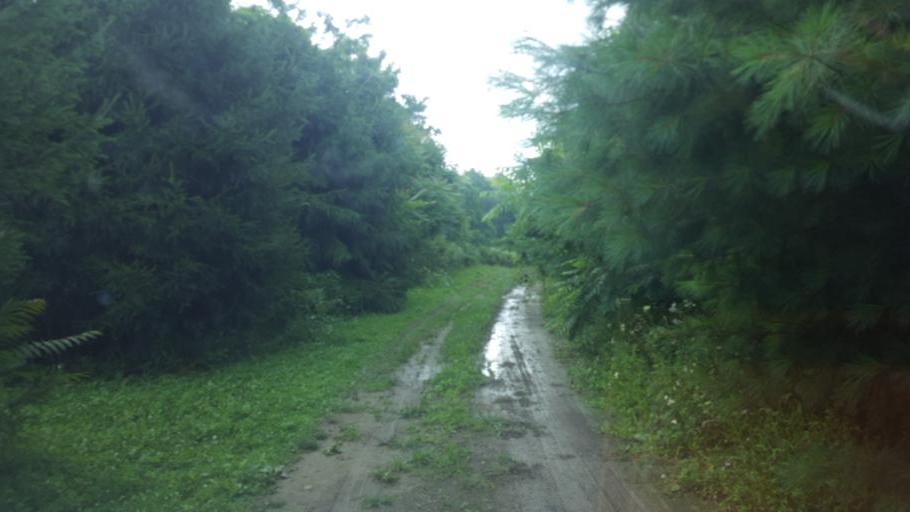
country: US
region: Ohio
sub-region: Columbiana County
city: Salineville
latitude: 40.5188
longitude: -80.8462
